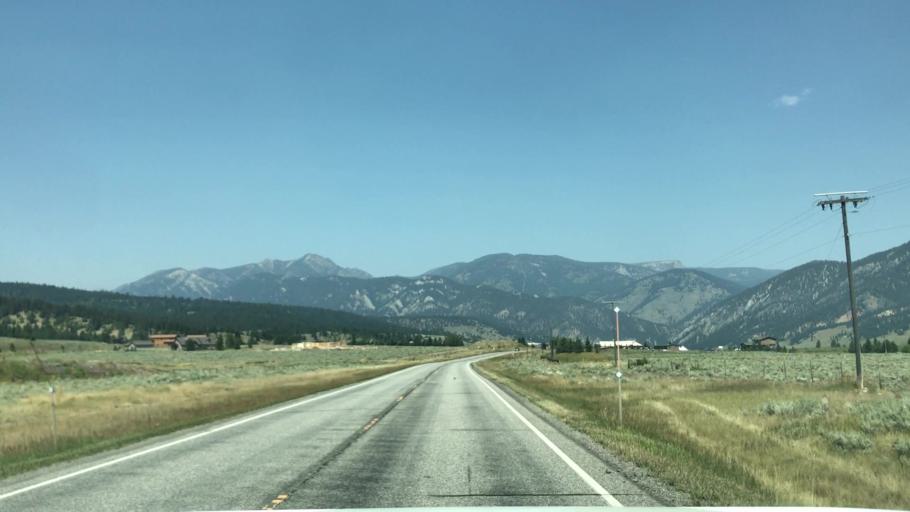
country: US
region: Montana
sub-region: Gallatin County
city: Big Sky
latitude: 45.2180
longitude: -111.2497
